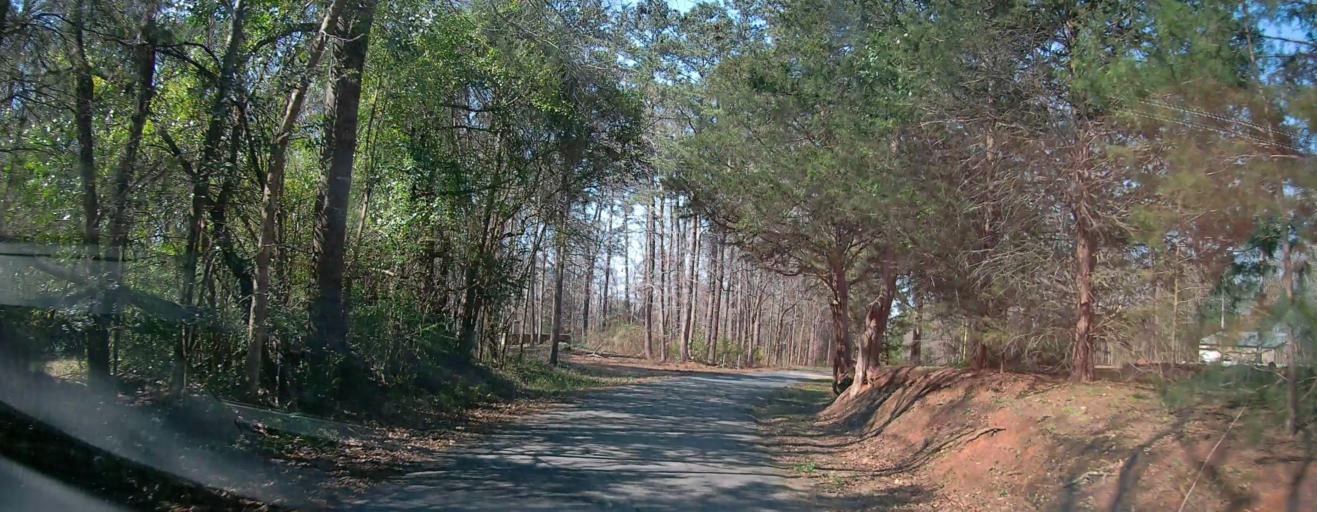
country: US
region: Georgia
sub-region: Jones County
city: Gray
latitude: 33.0021
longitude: -83.5595
